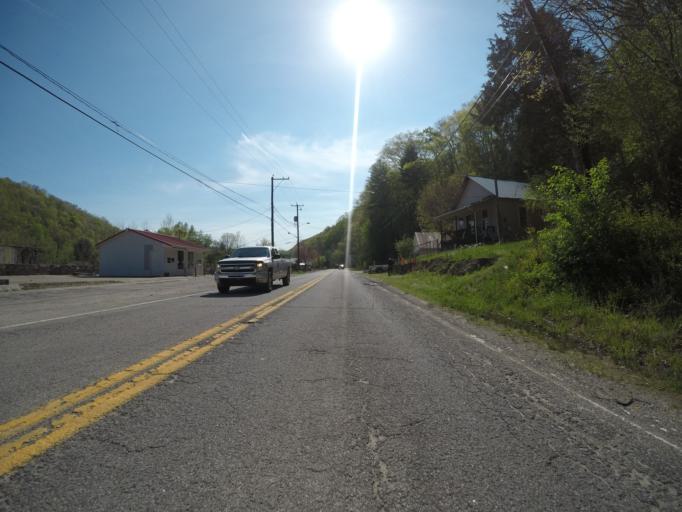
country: US
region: West Virginia
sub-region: Kanawha County
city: Clendenin
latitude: 38.4836
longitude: -81.3630
